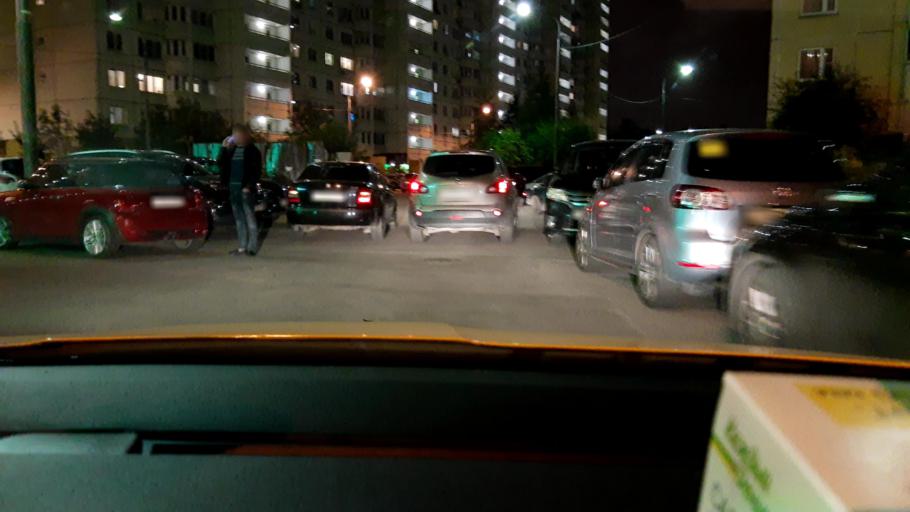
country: RU
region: Moskovskaya
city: Reutov
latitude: 55.7405
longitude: 37.8820
